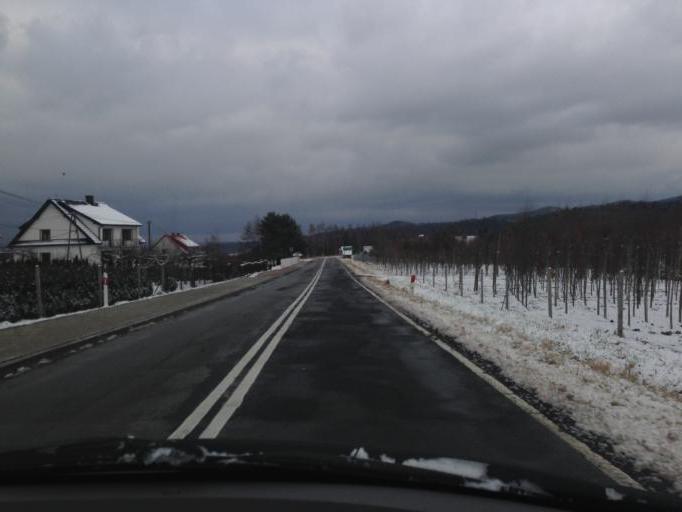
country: PL
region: Lesser Poland Voivodeship
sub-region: Powiat bochenski
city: Nowy Wisnicz
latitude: 49.8492
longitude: 20.5035
